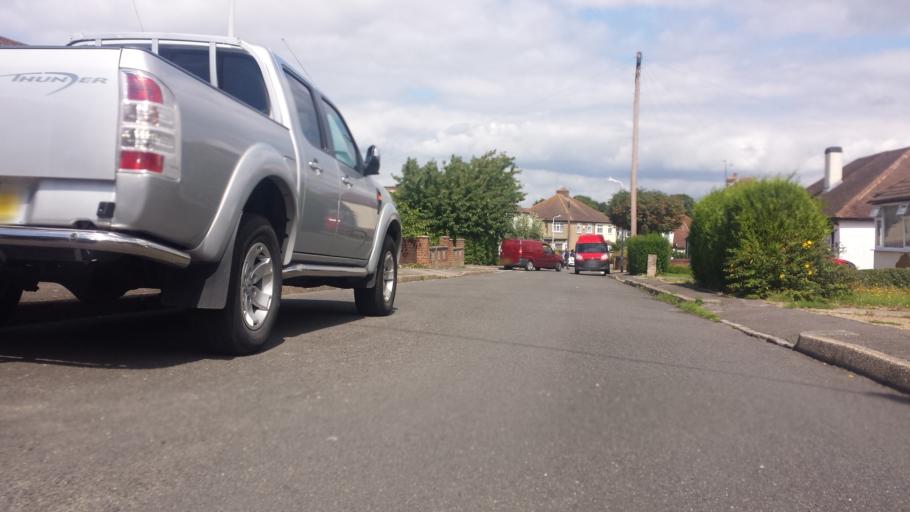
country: GB
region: England
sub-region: Kent
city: Swanley
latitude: 51.4017
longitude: 0.1605
